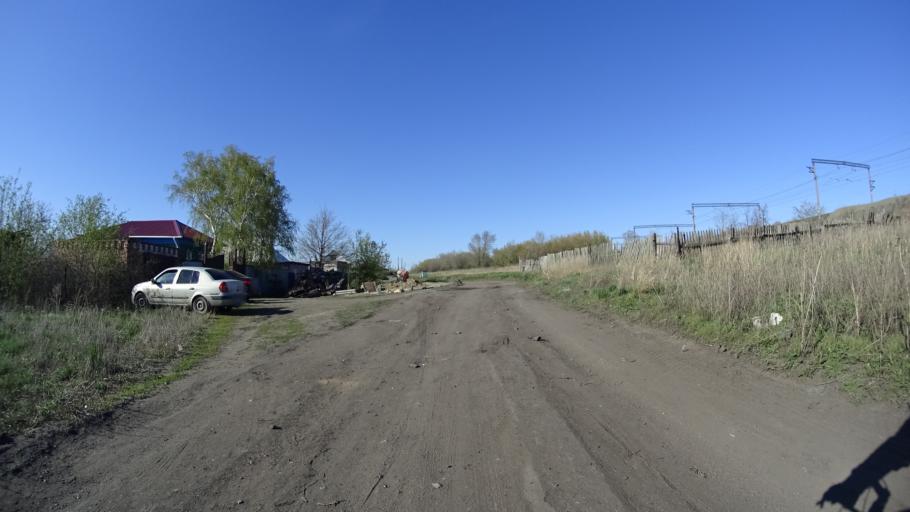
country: RU
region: Chelyabinsk
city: Troitsk
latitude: 54.0869
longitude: 61.5988
